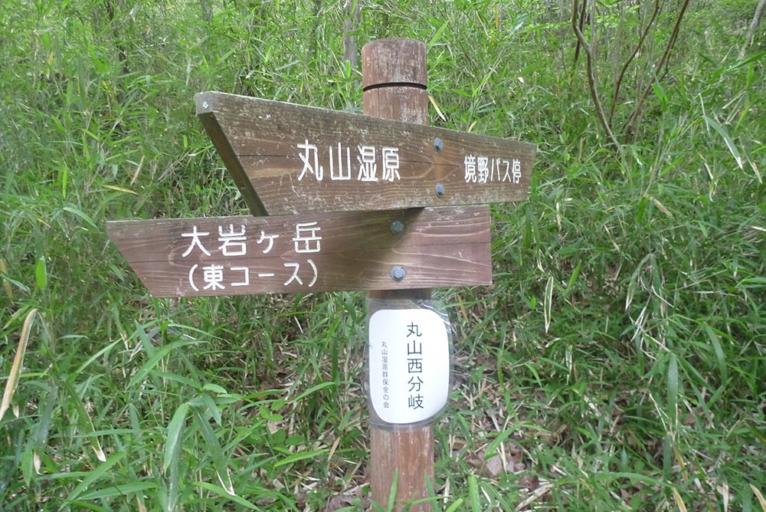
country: JP
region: Hyogo
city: Sandacho
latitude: 34.8830
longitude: 135.2886
